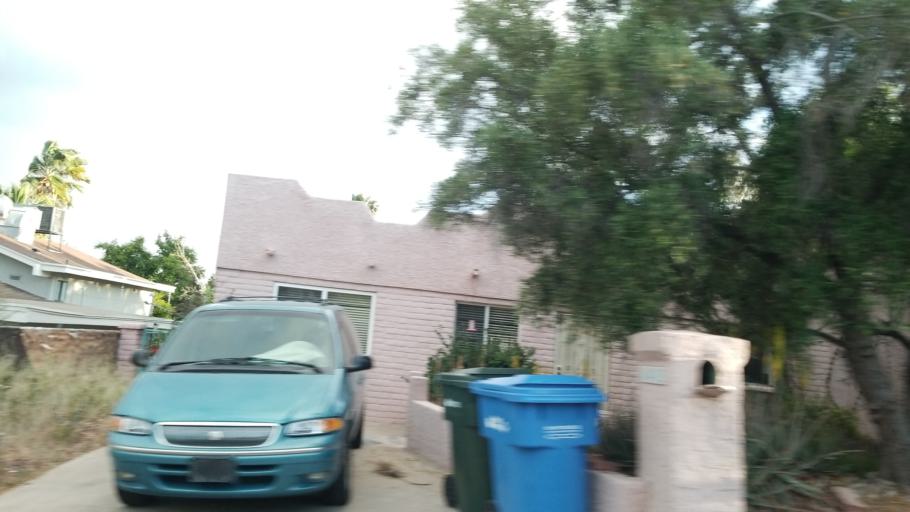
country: US
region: Arizona
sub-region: Maricopa County
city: Paradise Valley
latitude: 33.5911
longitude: -112.0517
